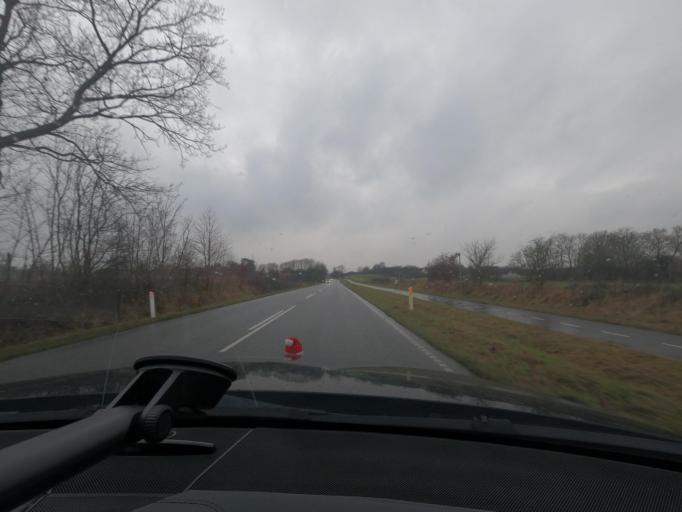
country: DK
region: South Denmark
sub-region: Sonderborg Kommune
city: Horuphav
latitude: 54.9059
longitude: 9.8543
